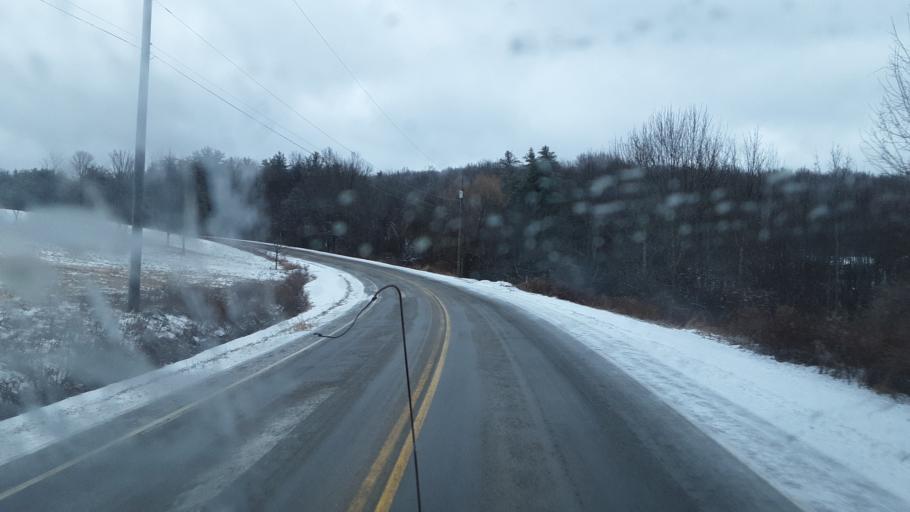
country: US
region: New York
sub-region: Allegany County
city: Friendship
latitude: 42.2458
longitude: -78.1475
